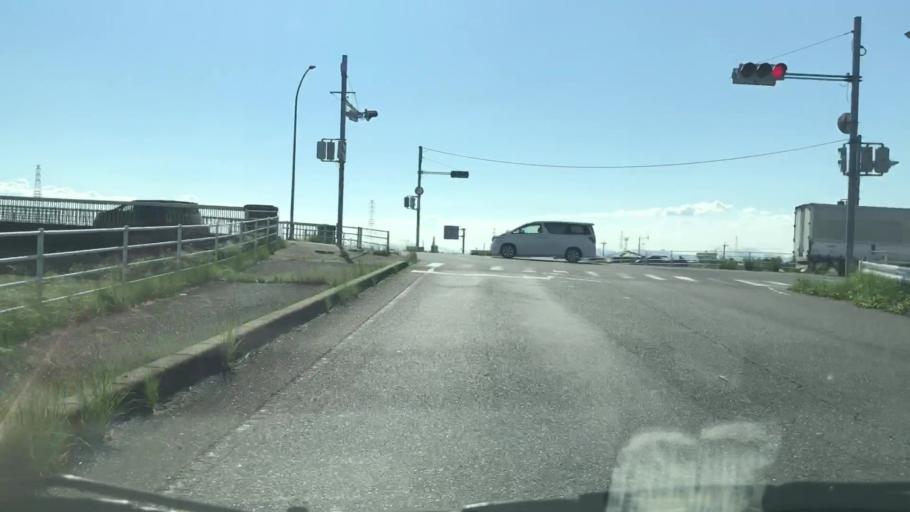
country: JP
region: Saga Prefecture
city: Kanzakimachi-kanzaki
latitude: 33.2513
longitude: 130.4061
